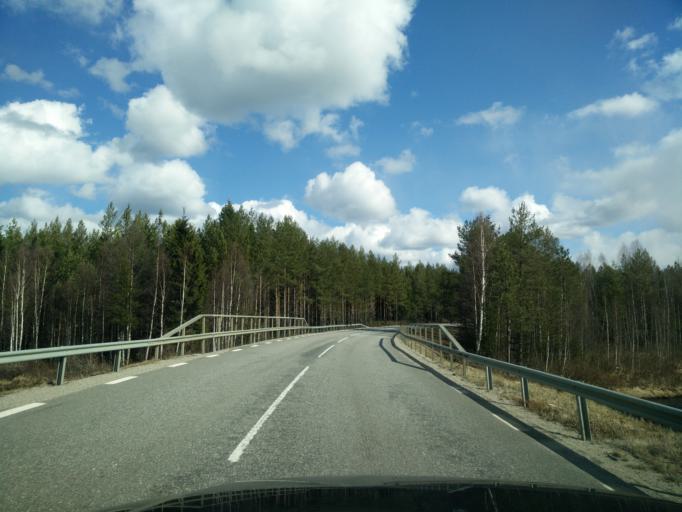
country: SE
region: Jaemtland
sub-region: Braecke Kommun
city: Braecke
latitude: 62.4589
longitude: 14.9649
